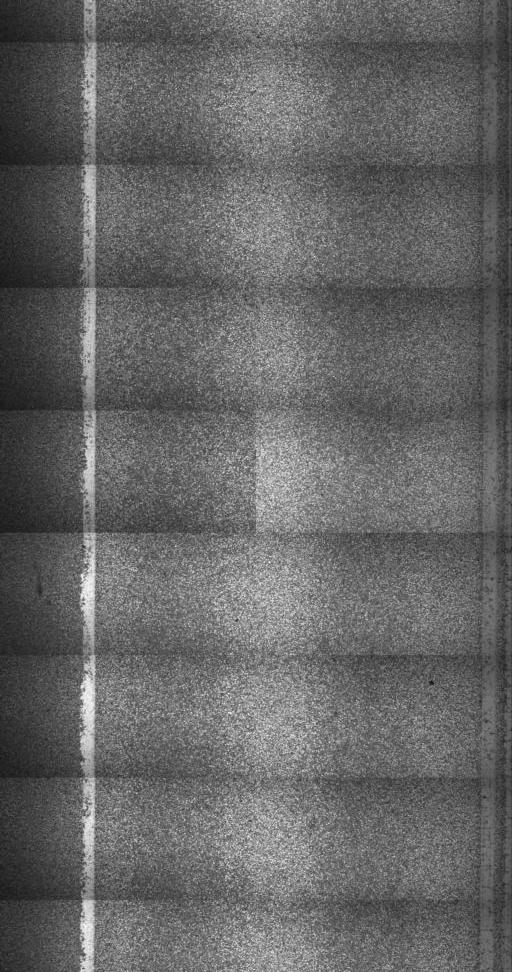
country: US
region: Vermont
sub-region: Lamoille County
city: Johnson
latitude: 44.5169
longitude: -72.7688
